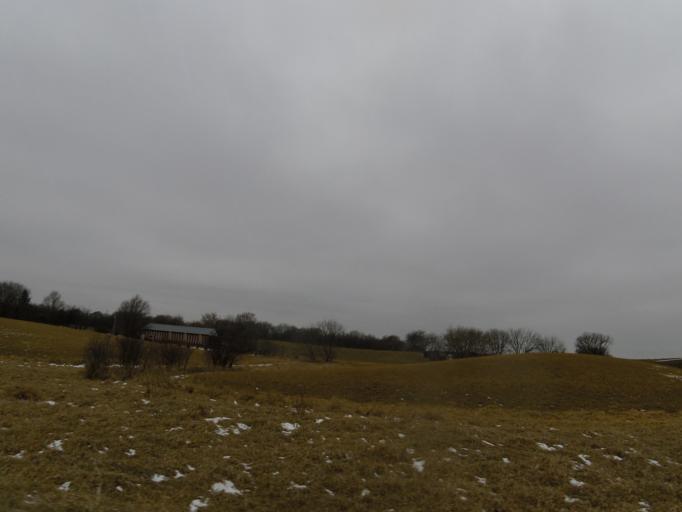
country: US
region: Minnesota
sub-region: Carver County
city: Watertown
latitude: 44.9776
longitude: -93.8493
